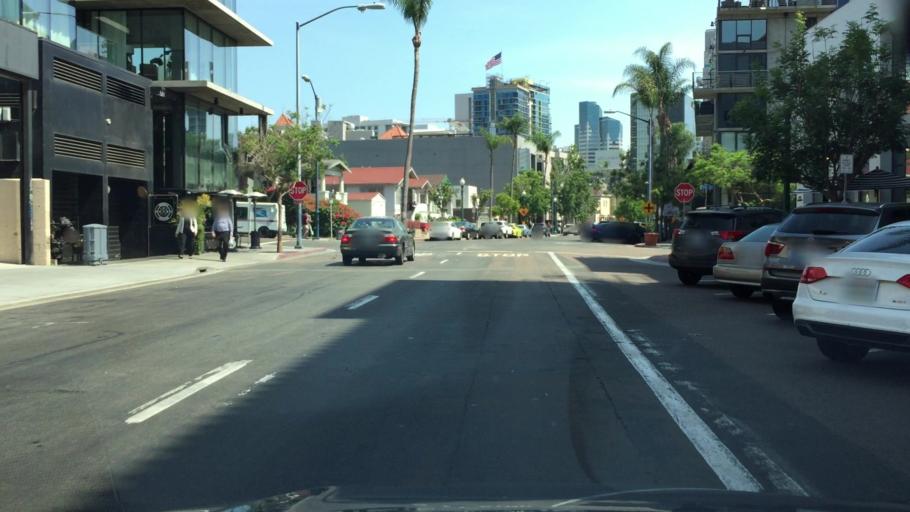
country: US
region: California
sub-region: San Diego County
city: San Diego
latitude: 32.7246
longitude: -117.1696
